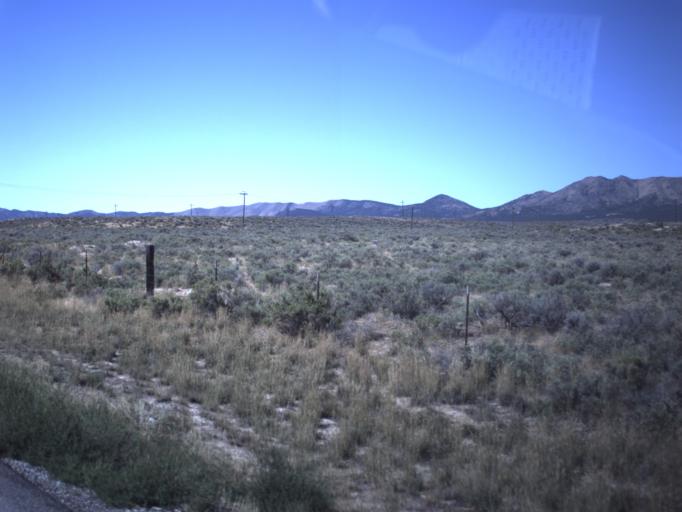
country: US
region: Utah
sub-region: Tooele County
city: Tooele
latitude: 40.1851
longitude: -112.4209
